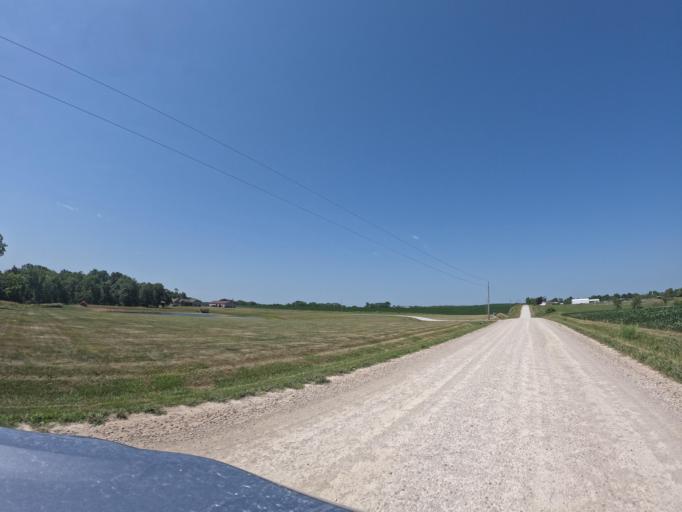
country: US
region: Iowa
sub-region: Henry County
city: Mount Pleasant
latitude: 40.8893
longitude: -91.5840
